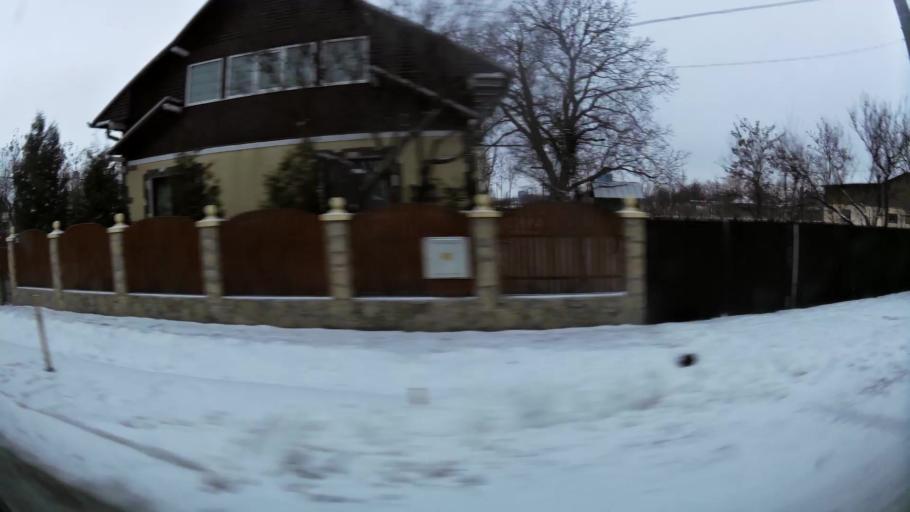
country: RO
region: Prahova
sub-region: Comuna Berceni
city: Corlatesti
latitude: 44.9105
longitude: 26.0897
